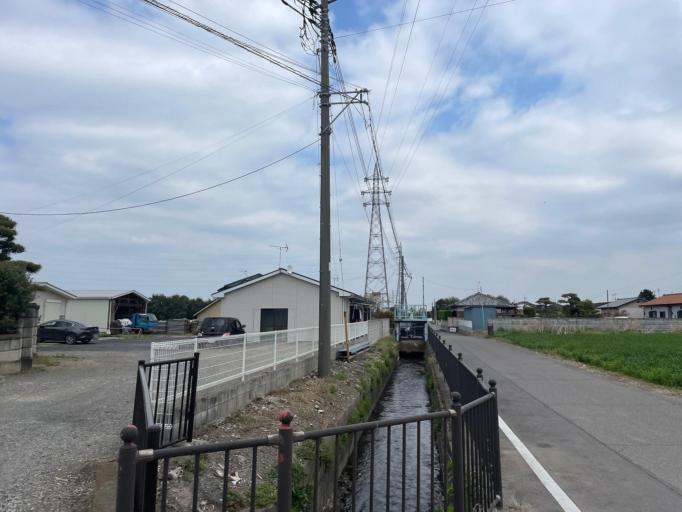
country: JP
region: Gunma
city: Isesaki
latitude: 36.2900
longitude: 139.1734
